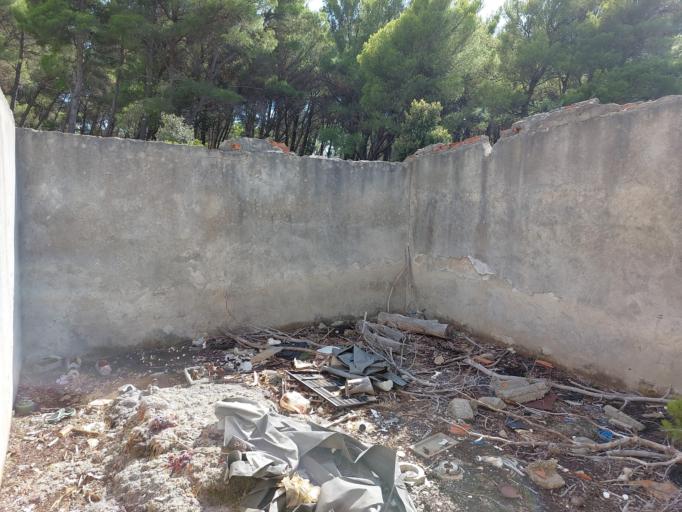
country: HR
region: Dubrovacko-Neretvanska
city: Smokvica
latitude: 42.7396
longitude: 16.8318
